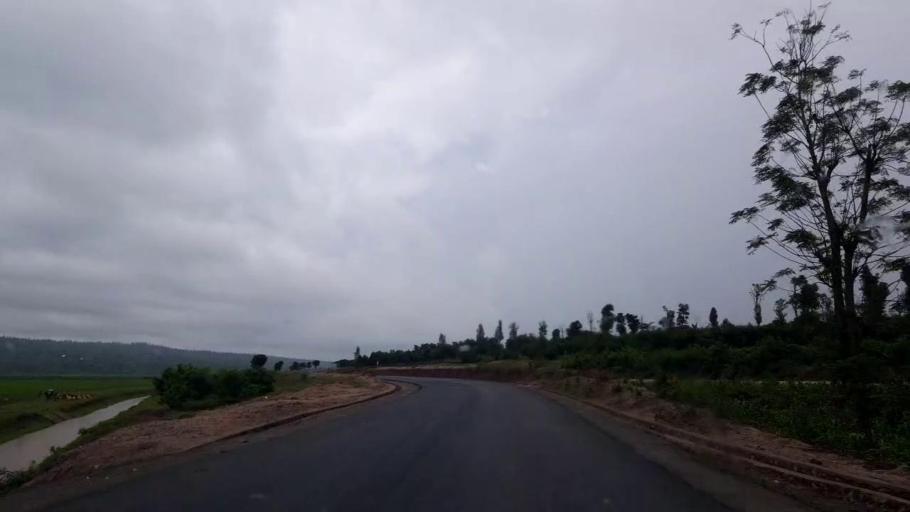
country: RW
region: Northern Province
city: Byumba
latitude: -1.4090
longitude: 30.2853
